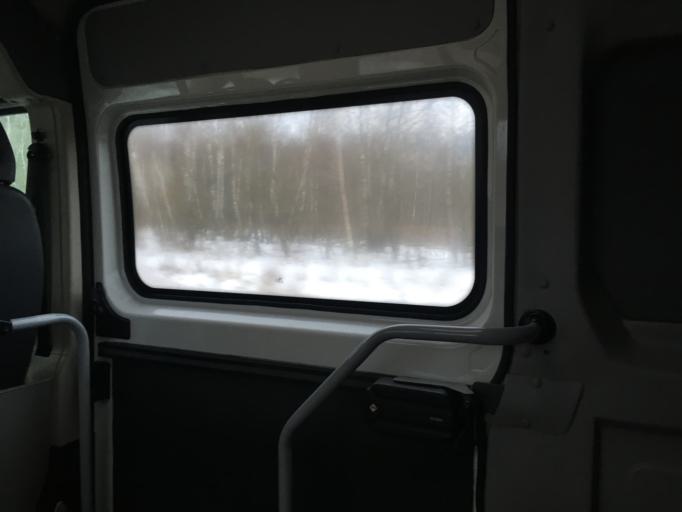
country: RU
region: Tula
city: Krapivna
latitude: 54.1250
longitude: 37.2448
